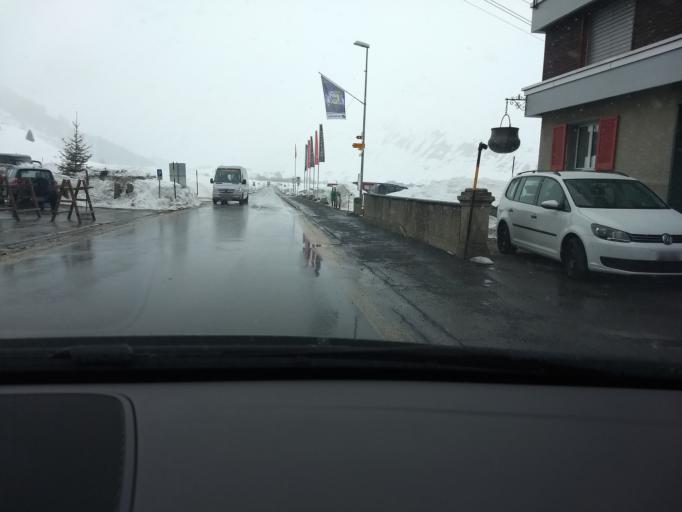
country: CH
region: Uri
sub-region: Uri
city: Andermatt
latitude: 46.6323
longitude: 8.5926
